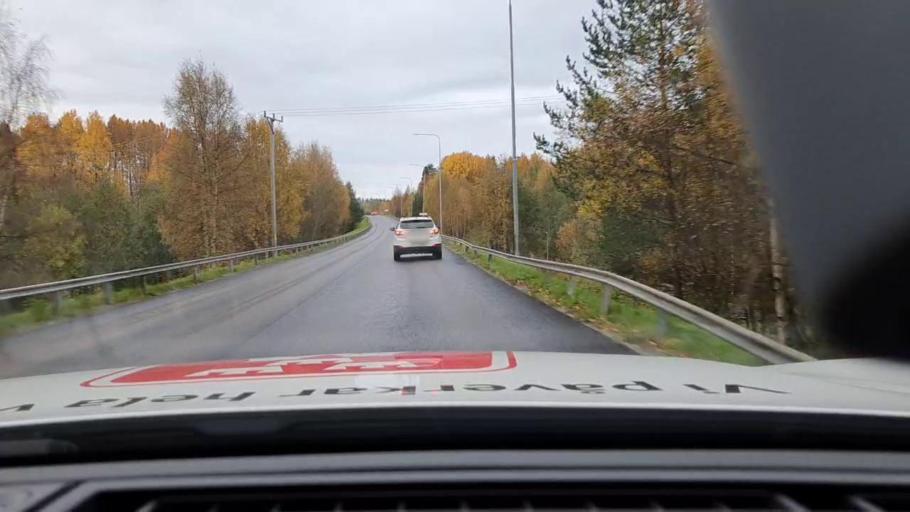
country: SE
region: Norrbotten
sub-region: Bodens Kommun
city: Saevast
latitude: 65.7664
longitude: 21.7392
